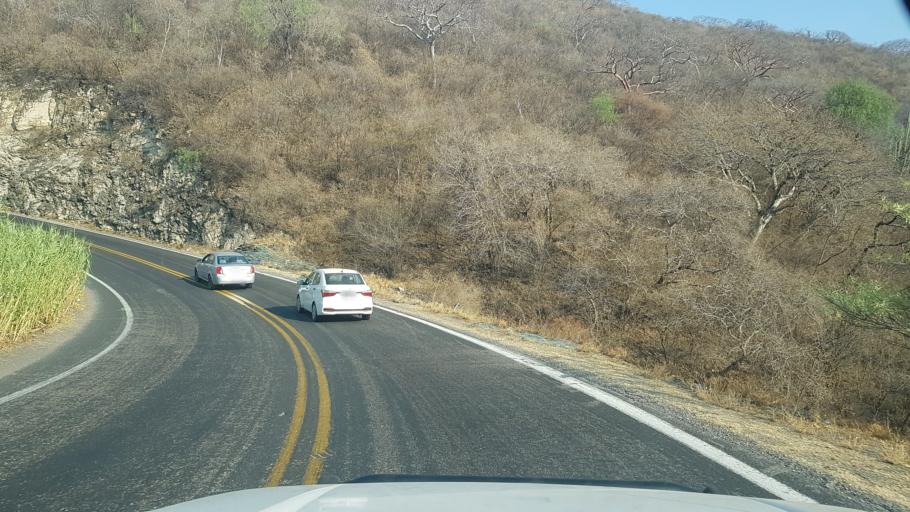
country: MX
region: Puebla
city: Calmeca
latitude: 18.6526
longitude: -98.6509
